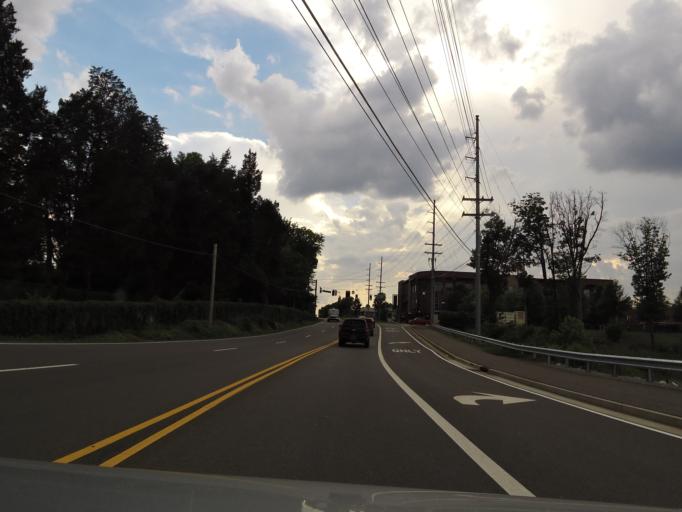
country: US
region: Tennessee
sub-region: Blount County
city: Louisville
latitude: 35.8570
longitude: -84.0780
